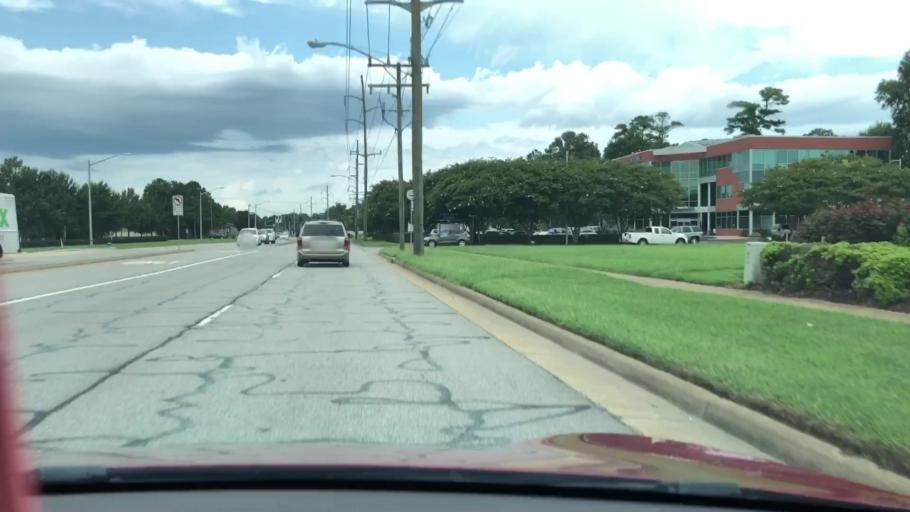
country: US
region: Virginia
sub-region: City of Virginia Beach
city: Virginia Beach
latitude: 36.8592
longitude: -76.0263
